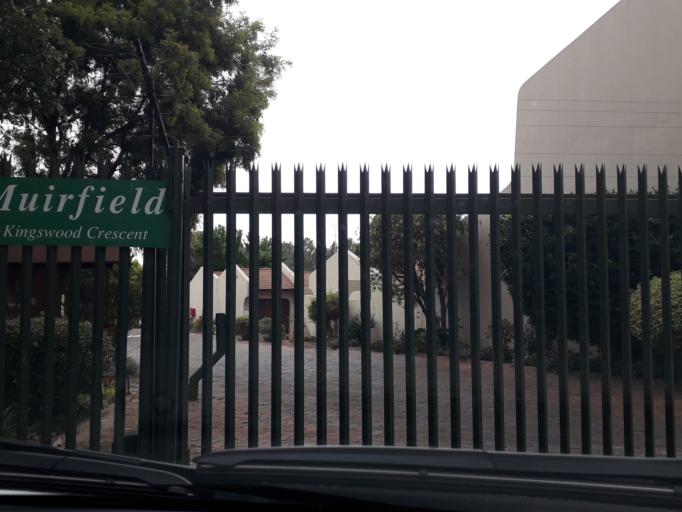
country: ZA
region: Gauteng
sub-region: City of Johannesburg Metropolitan Municipality
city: Johannesburg
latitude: -26.0813
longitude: 28.0321
